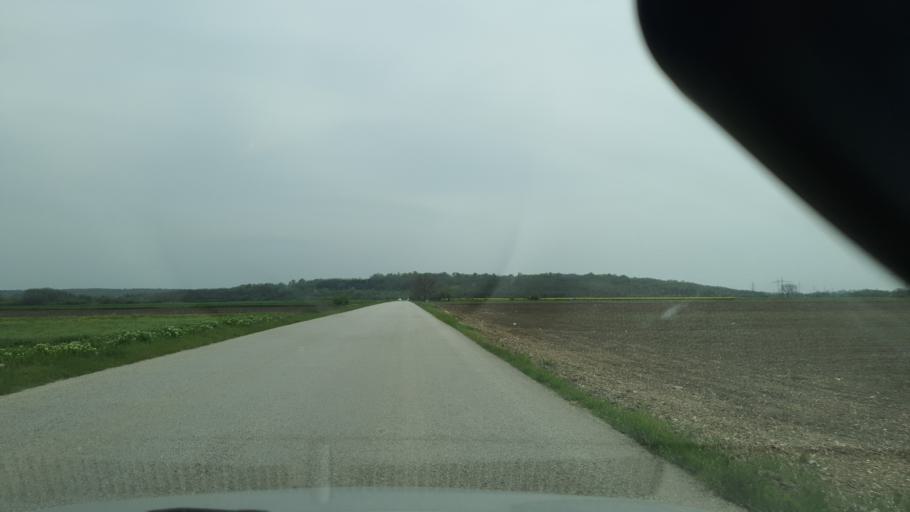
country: RS
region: Central Serbia
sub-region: Branicevski Okrug
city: Pozarevac
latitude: 44.6976
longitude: 21.1598
